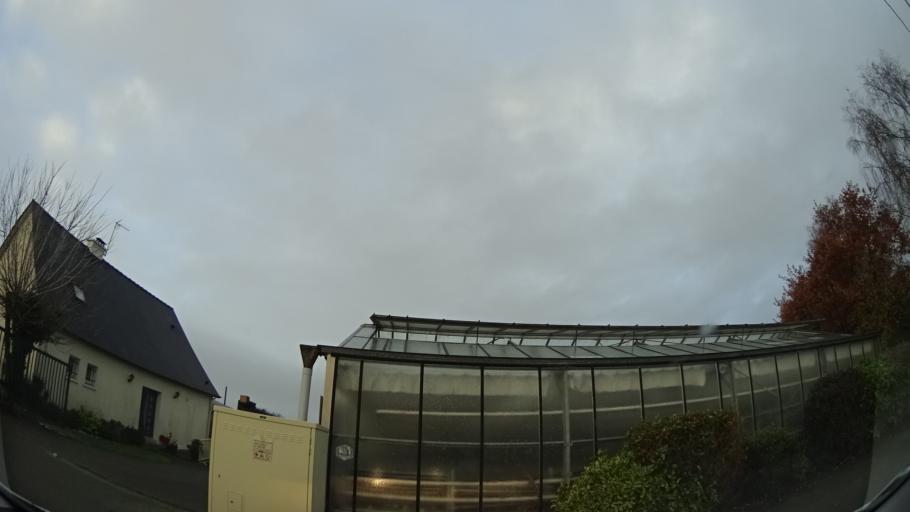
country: FR
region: Brittany
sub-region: Departement d'Ille-et-Vilaine
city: La Chapelle-des-Fougeretz
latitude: 48.1778
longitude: -1.7089
